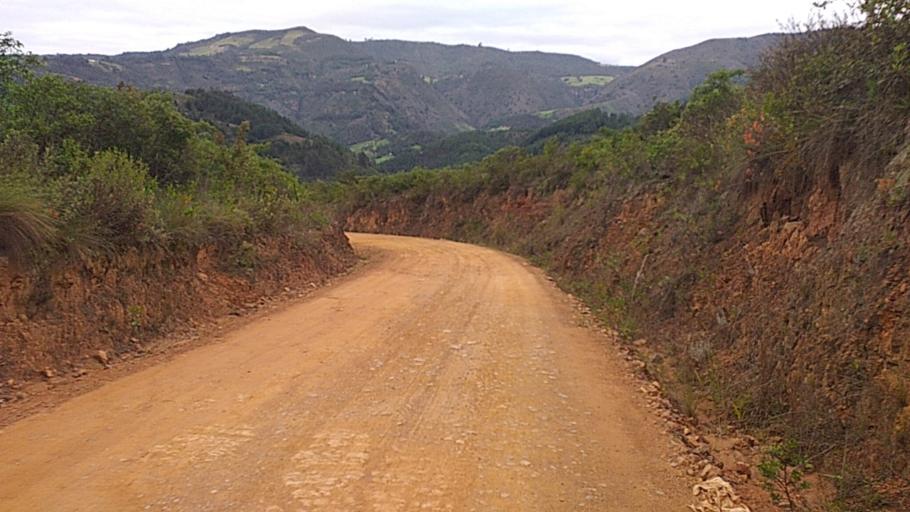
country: CO
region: Boyaca
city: Floresta
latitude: 5.8800
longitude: -72.9127
